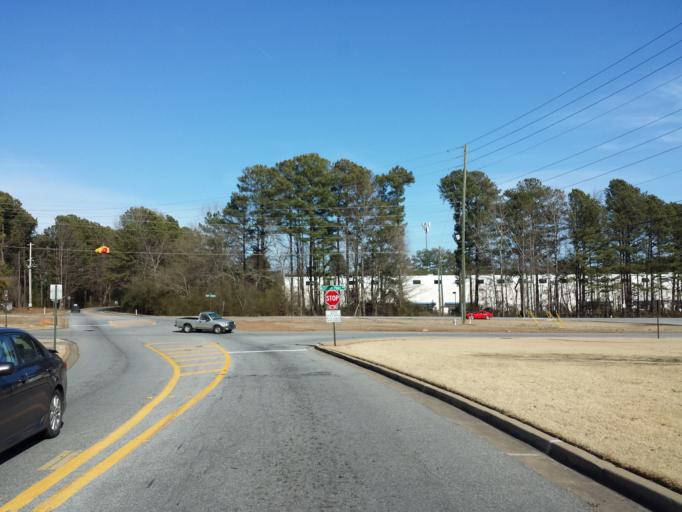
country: US
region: Georgia
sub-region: Cobb County
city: Kennesaw
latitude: 34.0288
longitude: -84.5911
